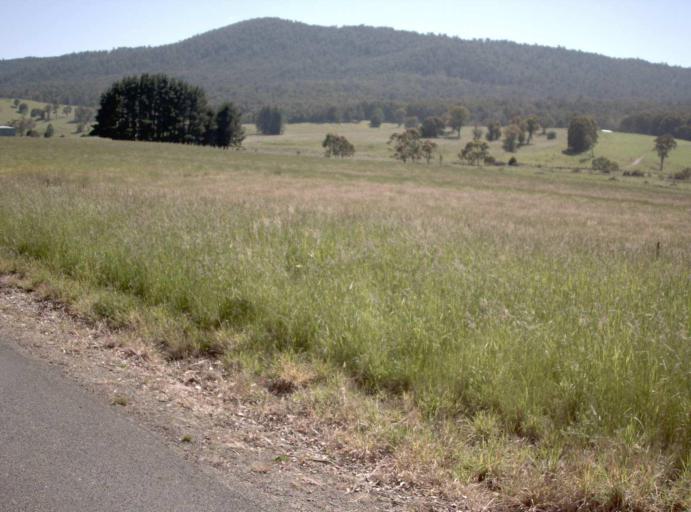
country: AU
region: New South Wales
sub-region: Bombala
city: Bombala
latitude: -37.1899
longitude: 148.7269
